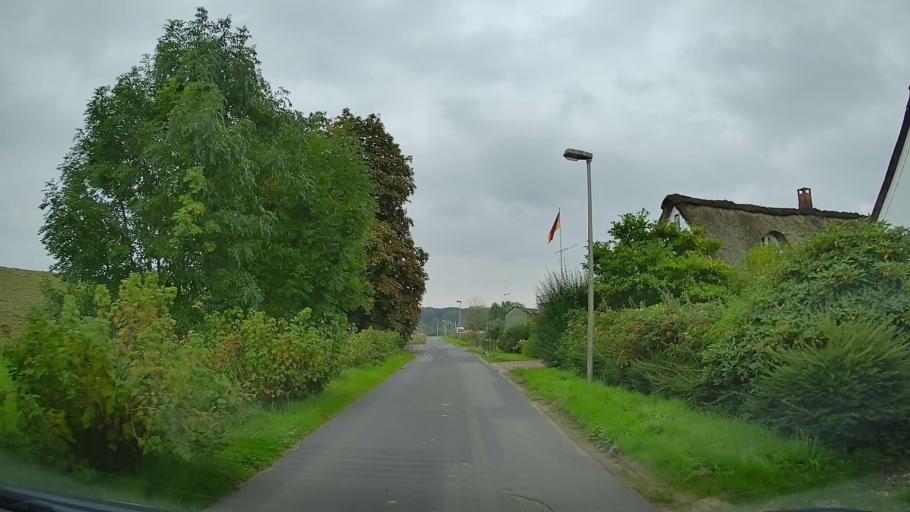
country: DE
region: Schleswig-Holstein
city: Kollmar
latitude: 53.6836
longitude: 9.4786
